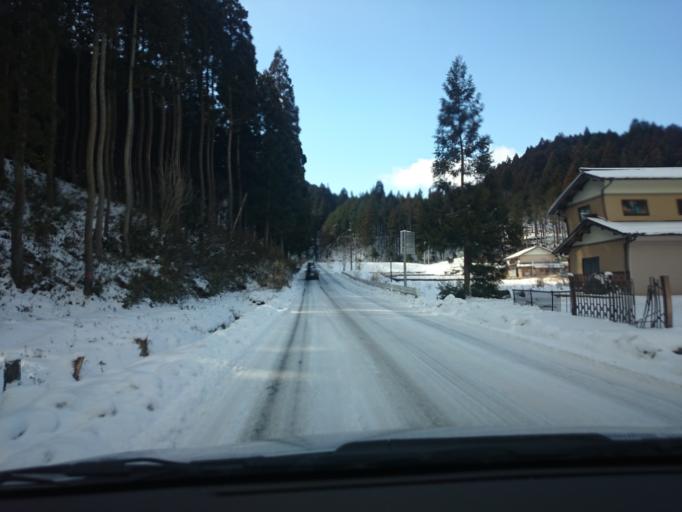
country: JP
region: Gifu
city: Gujo
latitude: 35.7373
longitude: 136.9936
